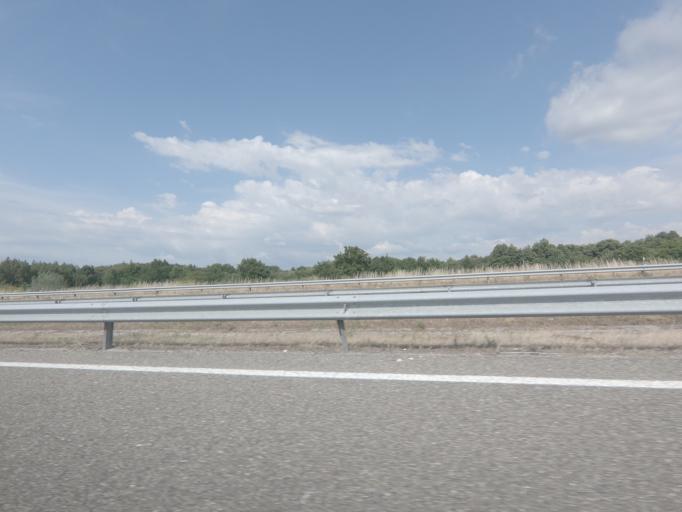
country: ES
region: Galicia
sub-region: Provincia de Ourense
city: Taboadela
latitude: 42.2639
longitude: -7.8688
